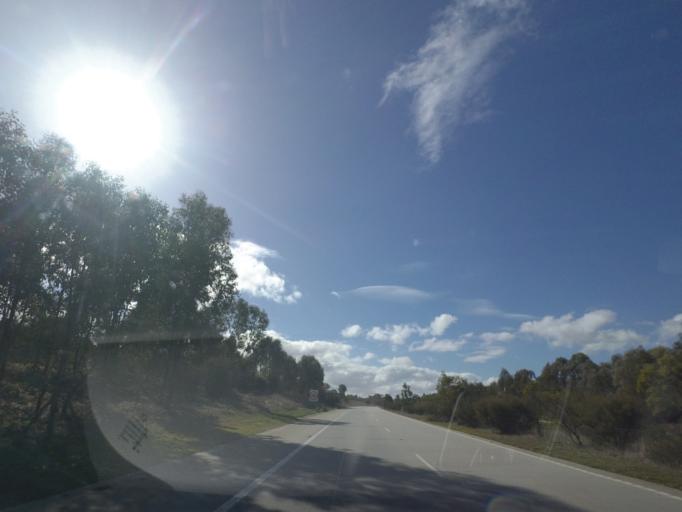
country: AU
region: New South Wales
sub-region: Albury Municipality
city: Lavington
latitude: -36.0313
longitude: 146.9765
